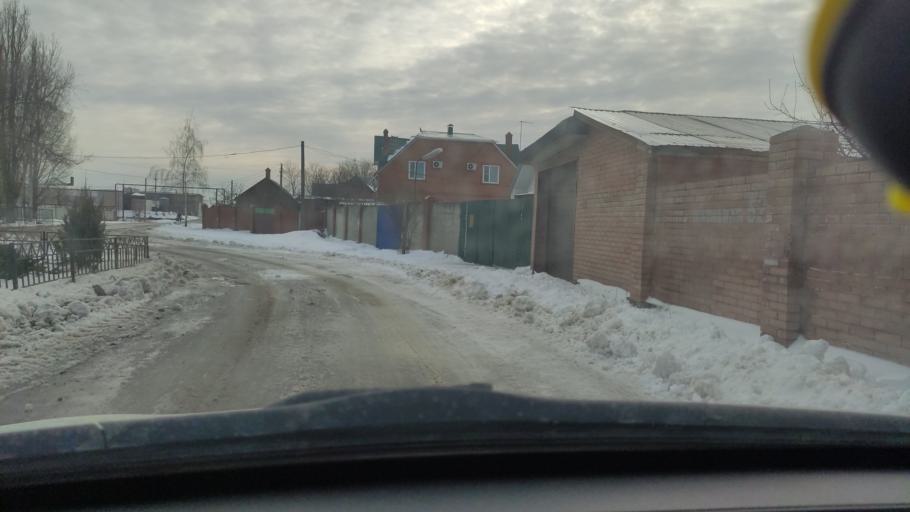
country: RU
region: Samara
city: Tol'yatti
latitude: 53.5632
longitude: 49.3935
